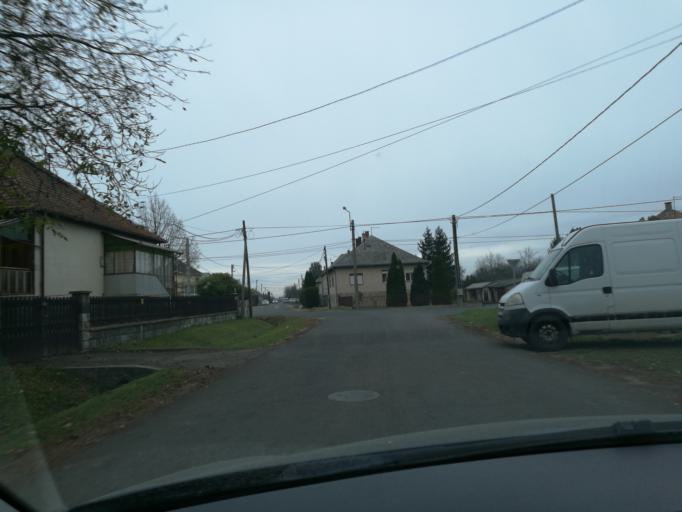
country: HU
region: Nograd
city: Szecseny
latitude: 48.0750
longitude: 19.5286
